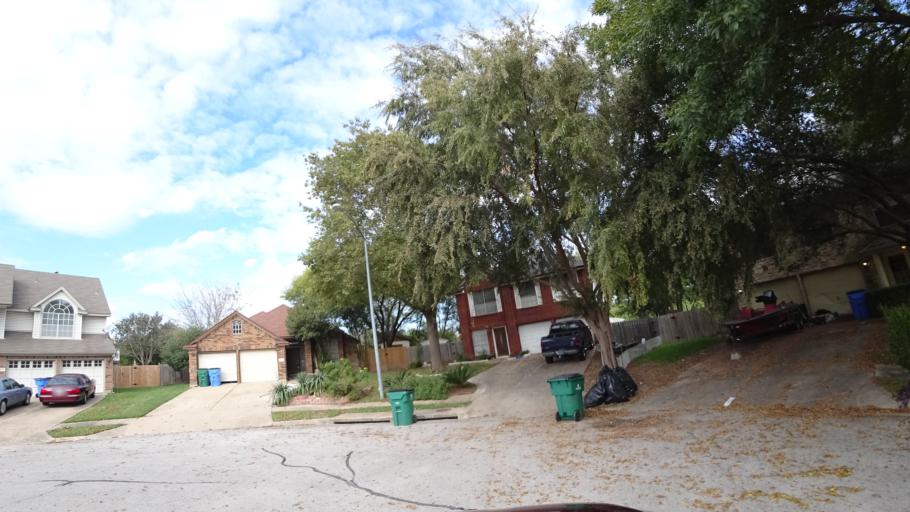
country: US
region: Texas
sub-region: Travis County
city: Pflugerville
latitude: 30.4418
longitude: -97.6350
